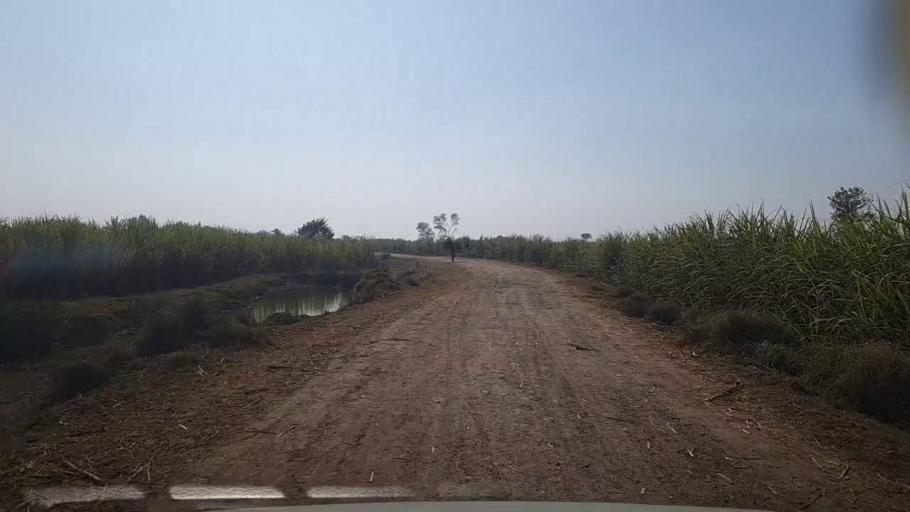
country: PK
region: Sindh
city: Khairpur
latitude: 28.0702
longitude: 69.6176
